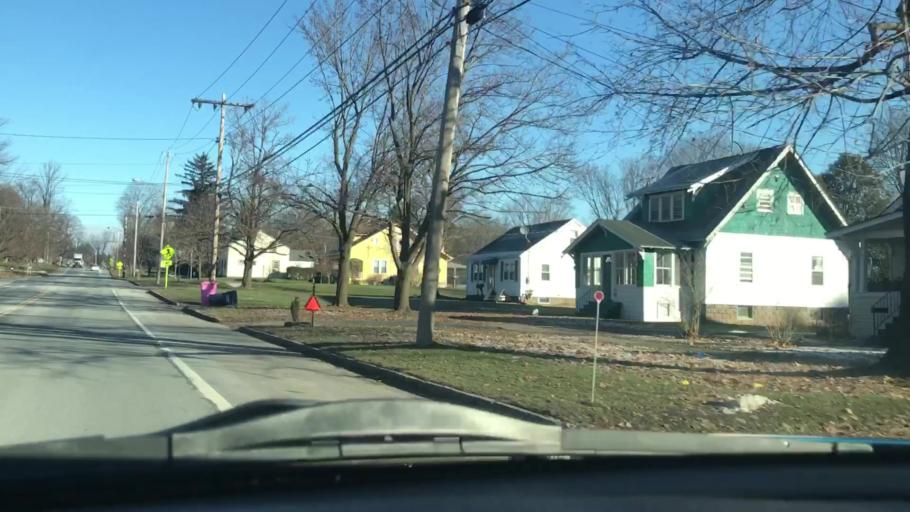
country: US
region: New York
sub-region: Madison County
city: Oneida
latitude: 43.0833
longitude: -75.6335
